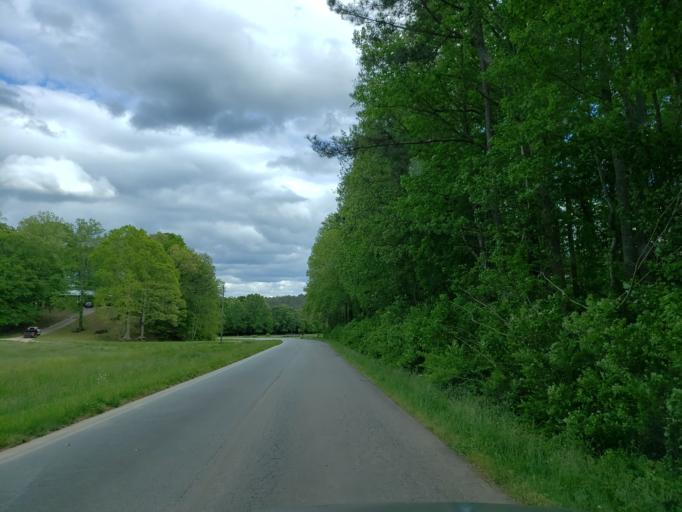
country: US
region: Georgia
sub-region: Haralson County
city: Tallapoosa
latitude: 33.7863
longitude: -85.3371
